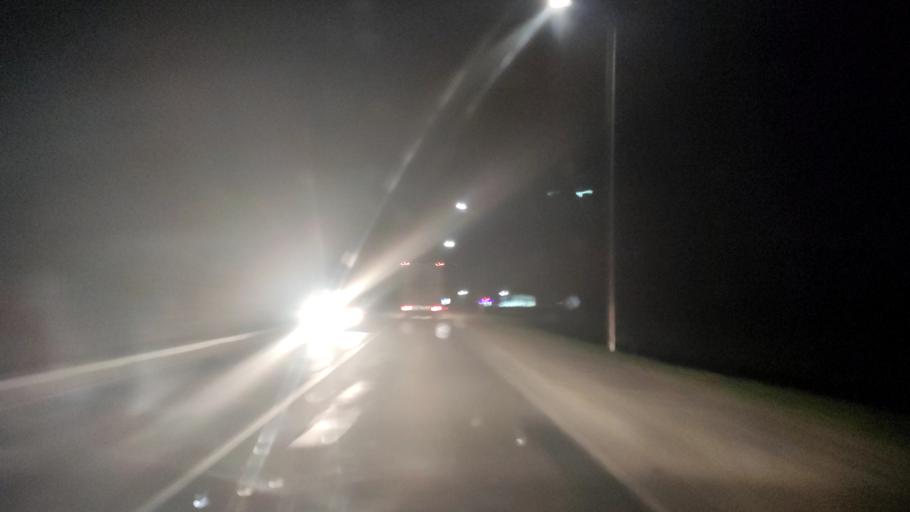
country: RU
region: Kursk
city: Gorshechnoye
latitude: 51.5300
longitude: 38.0226
